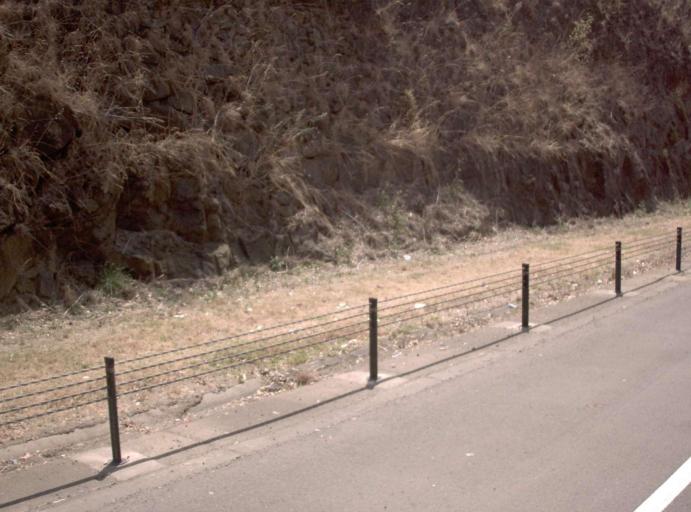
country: AU
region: Victoria
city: Abbotsford
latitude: -37.7933
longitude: 145.0070
